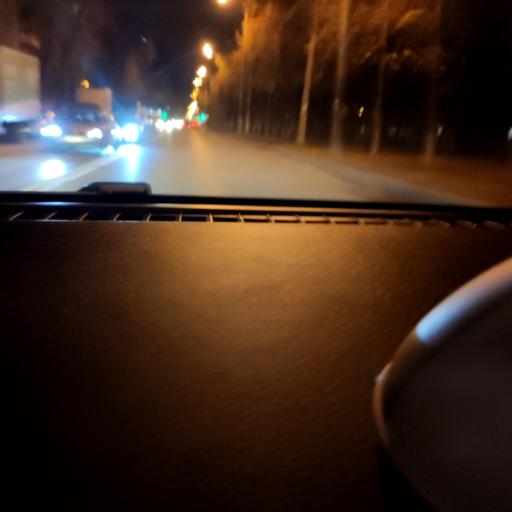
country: RU
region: Samara
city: Samara
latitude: 53.2061
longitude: 50.2385
